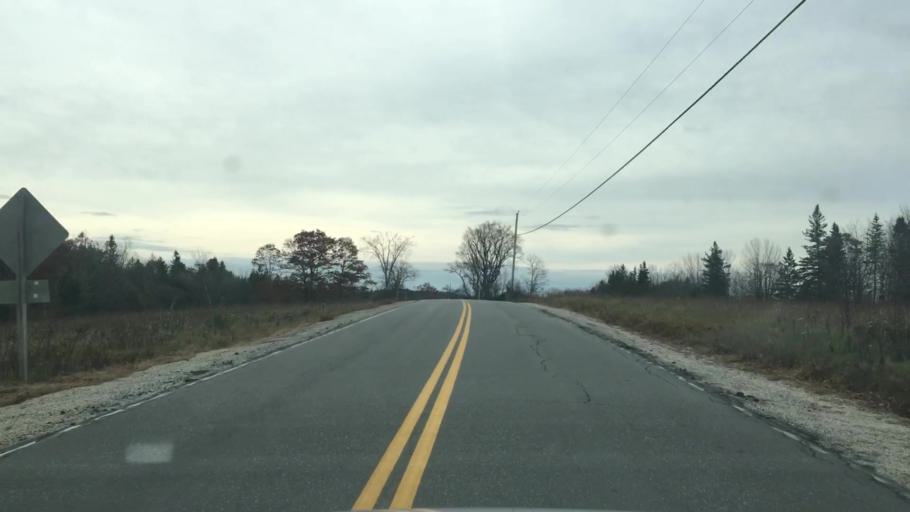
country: US
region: Maine
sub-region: Hancock County
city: Penobscot
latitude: 44.4412
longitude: -68.6359
